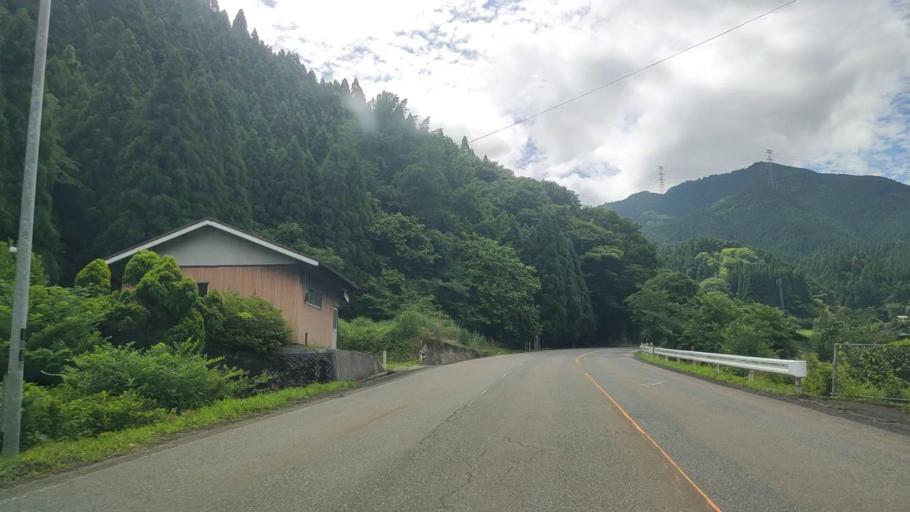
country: JP
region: Okayama
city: Niimi
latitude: 35.2072
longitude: 133.4937
